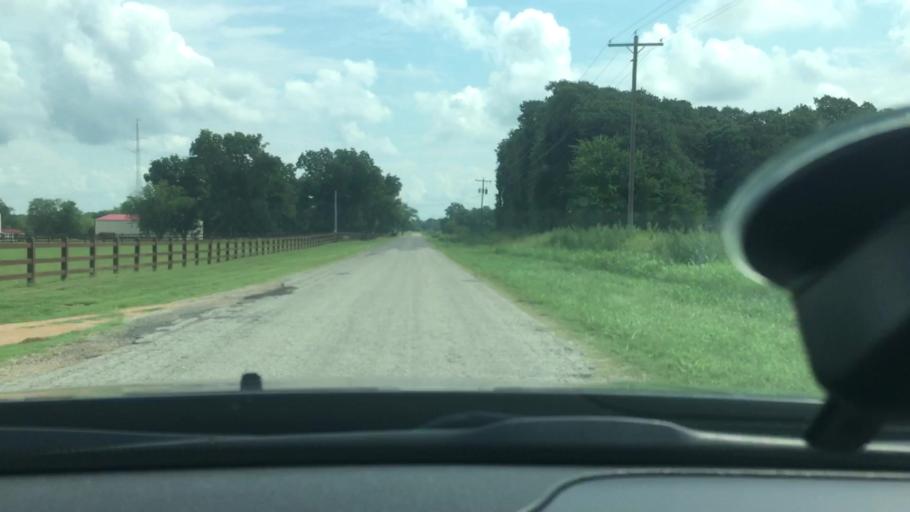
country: US
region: Oklahoma
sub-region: Carter County
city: Dickson
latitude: 34.2271
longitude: -96.8957
